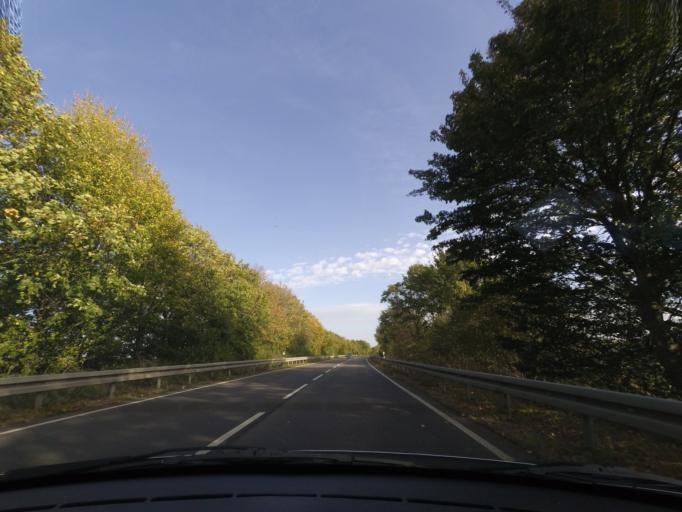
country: DE
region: North Rhine-Westphalia
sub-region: Regierungsbezirk Dusseldorf
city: Neubrueck
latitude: 51.1672
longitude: 6.6418
